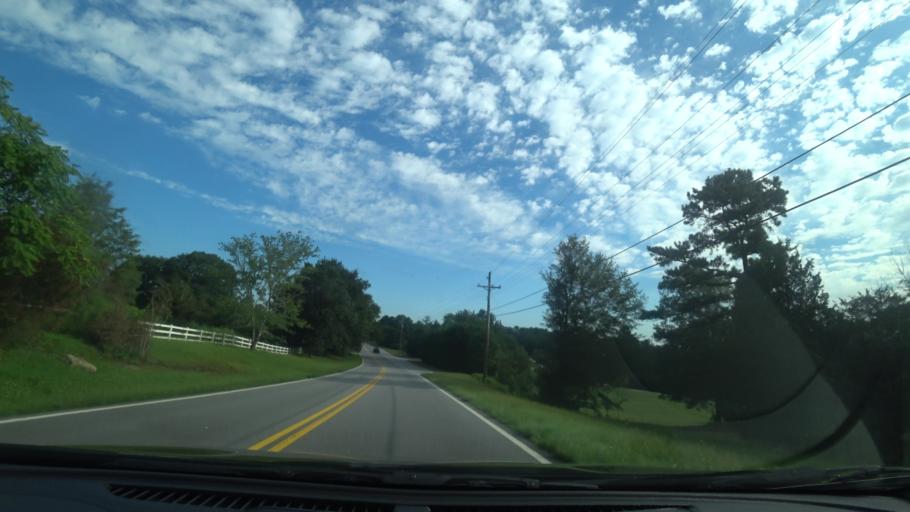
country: US
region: Georgia
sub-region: Rockdale County
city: Lakeview Estates
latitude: 33.7562
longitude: -83.9829
